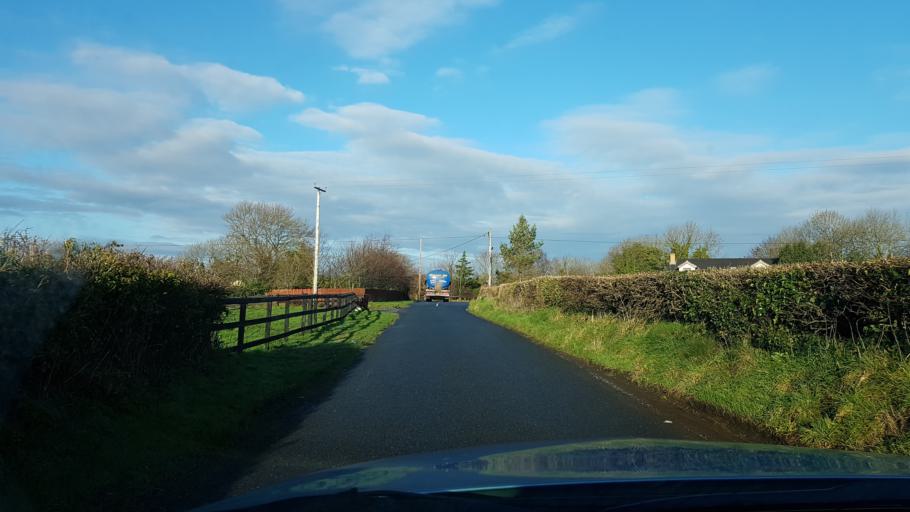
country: GB
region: Northern Ireland
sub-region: Ards District
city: Greyabbey
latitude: 54.5566
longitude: -5.5478
